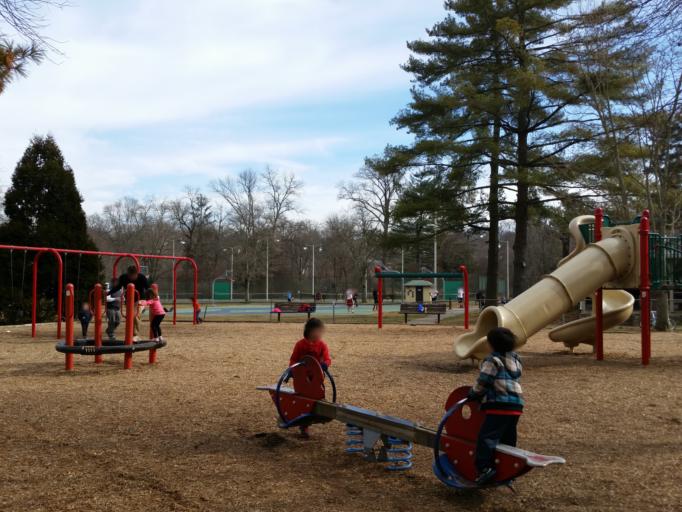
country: US
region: Maryland
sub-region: Montgomery County
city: Chevy Chase
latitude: 38.9871
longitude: -77.0620
